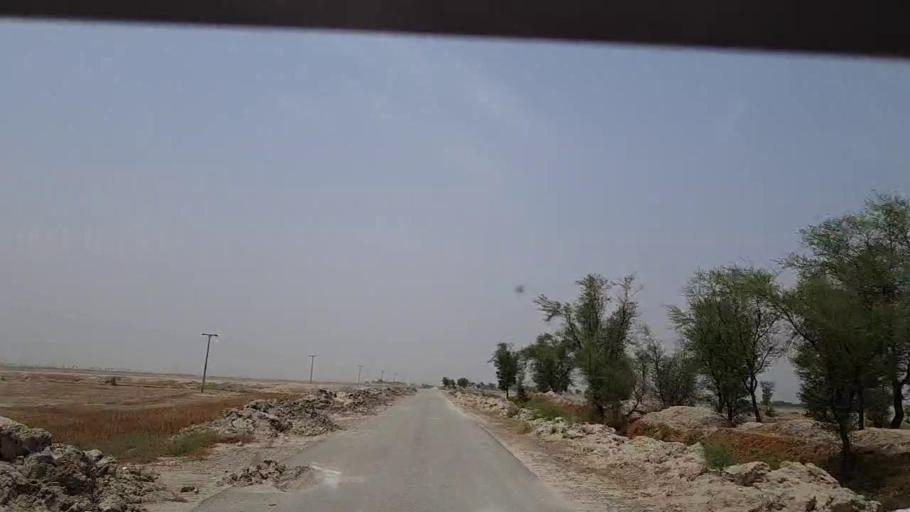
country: PK
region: Sindh
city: Khairpur Nathan Shah
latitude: 27.0322
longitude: 67.6197
